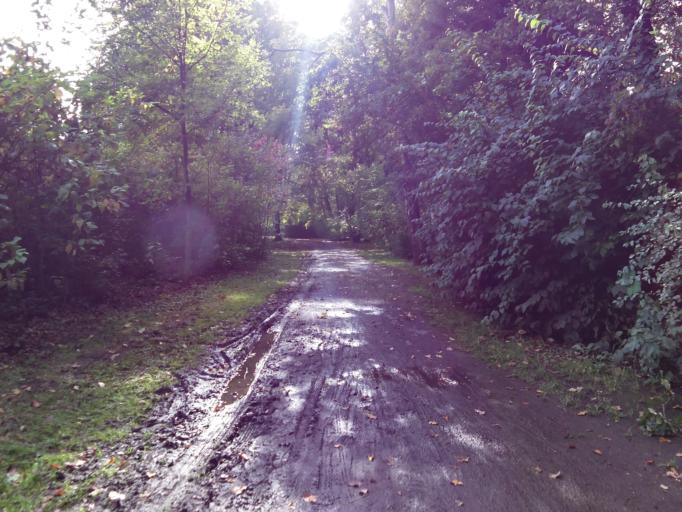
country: DE
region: Saxony
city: Leipzig
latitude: 51.3061
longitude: 12.4212
